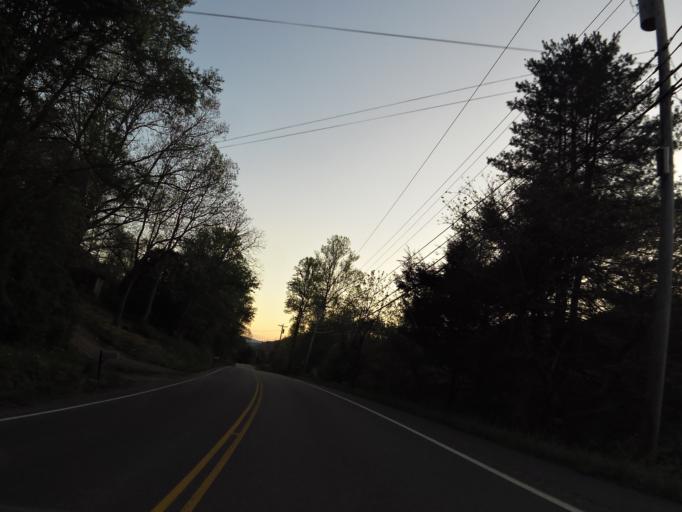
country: US
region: Tennessee
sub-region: Campbell County
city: LaFollette
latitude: 36.4021
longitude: -84.1193
